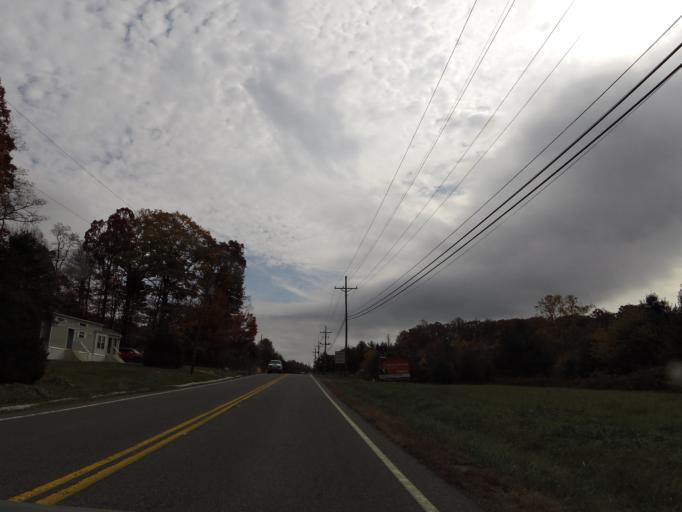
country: US
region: Virginia
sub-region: Carroll County
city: Cana
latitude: 36.6722
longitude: -80.6943
